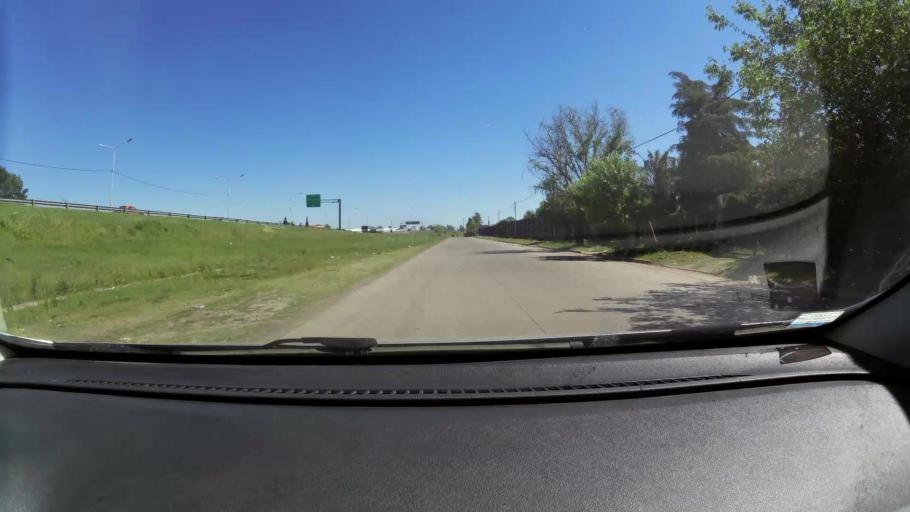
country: AR
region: Santa Fe
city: Perez
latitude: -32.9641
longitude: -60.7193
